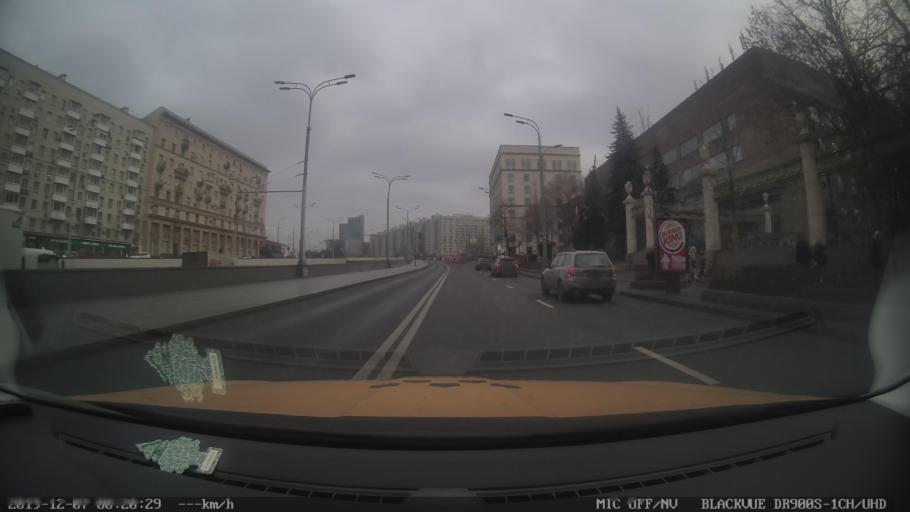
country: RU
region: Moscow
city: Novokhovrino
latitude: 55.8698
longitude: 37.4974
